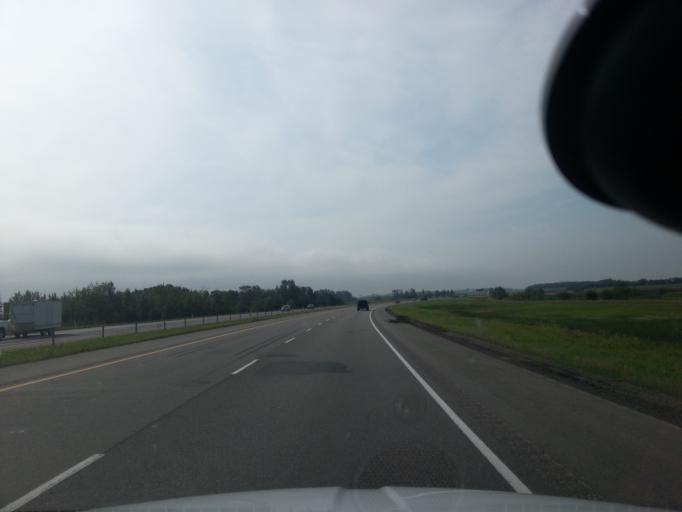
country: CA
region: Alberta
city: Penhold
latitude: 52.1822
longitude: -113.8156
